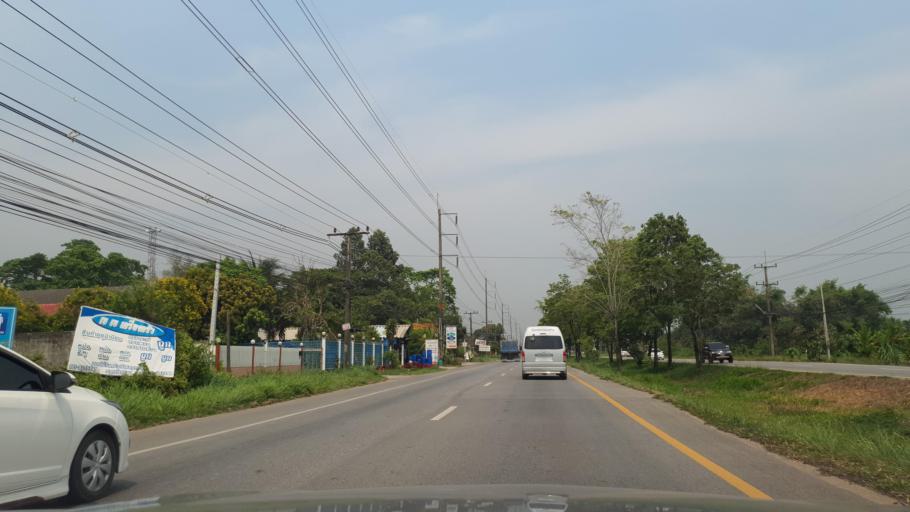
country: TH
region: Rayong
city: Rayong
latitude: 12.6404
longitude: 101.3940
